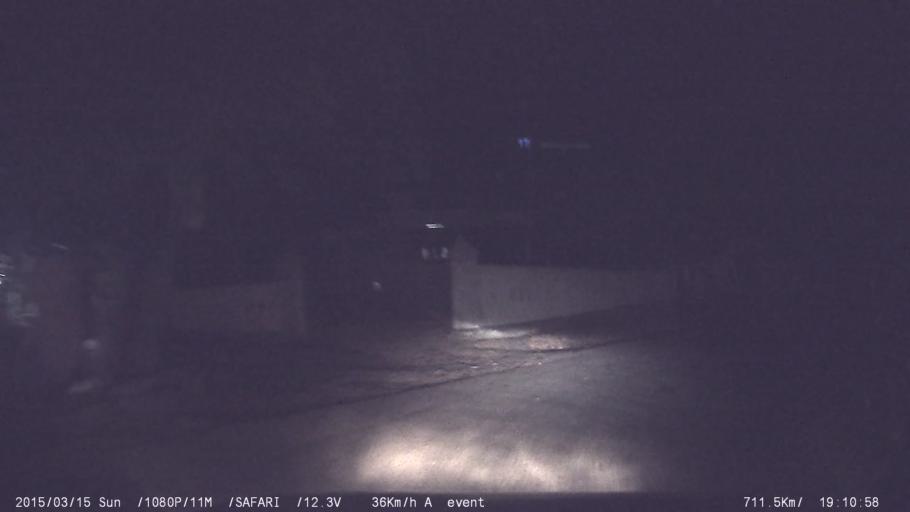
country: IN
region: Kerala
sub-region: Ernakulam
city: Piravam
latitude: 9.8718
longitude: 76.6154
